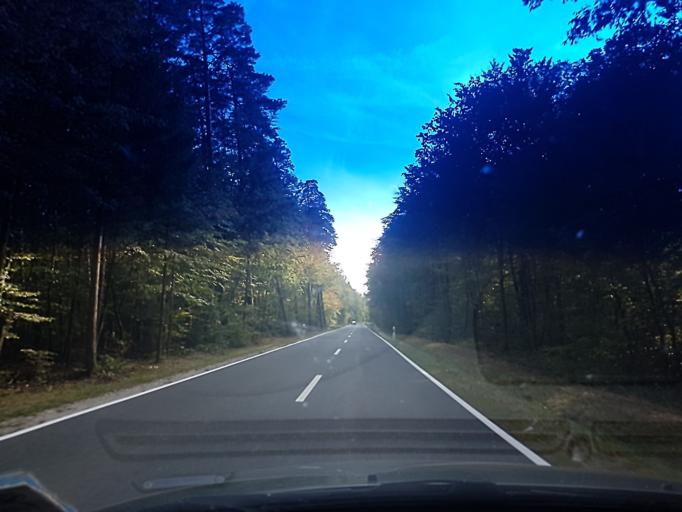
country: DE
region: Bavaria
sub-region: Upper Franconia
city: Burgwindheim
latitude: 49.7933
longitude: 10.5721
